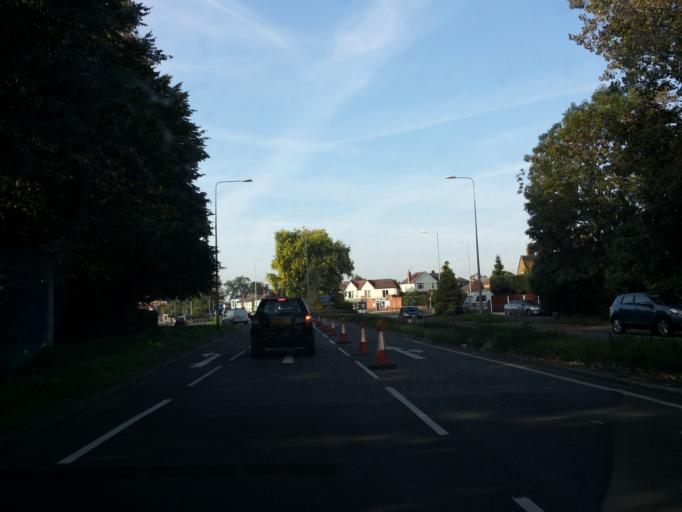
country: GB
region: England
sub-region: Staffordshire
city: Stone
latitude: 52.8959
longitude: -2.1484
